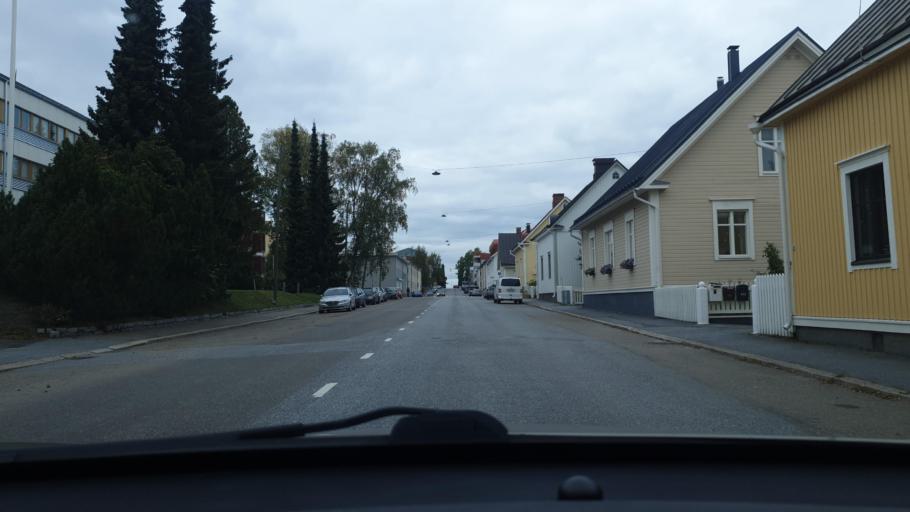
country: FI
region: Ostrobothnia
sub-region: Vaasa
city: Vaasa
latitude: 63.0876
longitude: 21.6295
